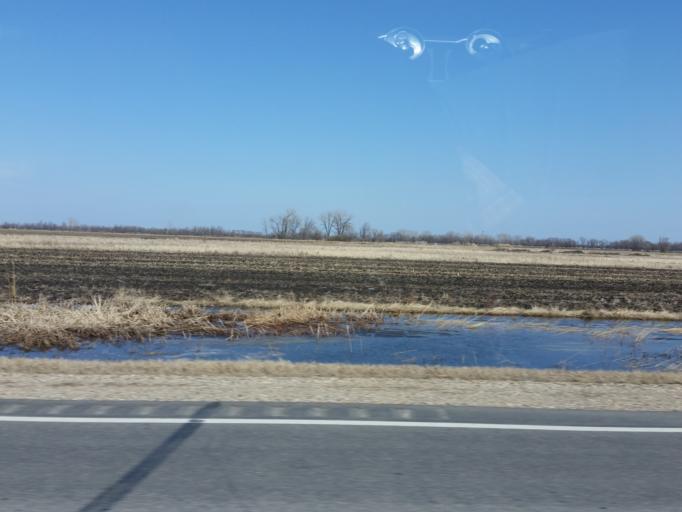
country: US
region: North Dakota
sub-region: Grand Forks County
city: Grand Forks Air Force Base
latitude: 48.1269
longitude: -97.2387
